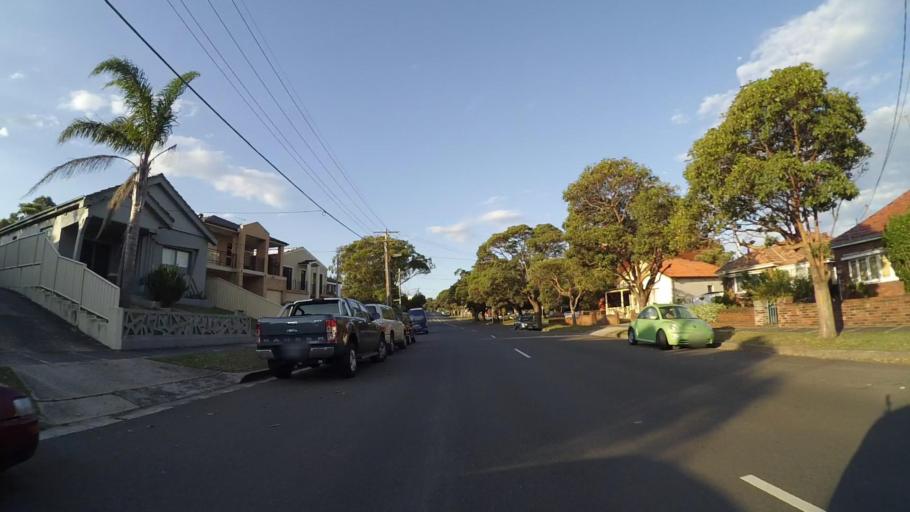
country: AU
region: New South Wales
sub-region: Randwick
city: Daceyville
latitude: -33.9292
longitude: 151.2326
